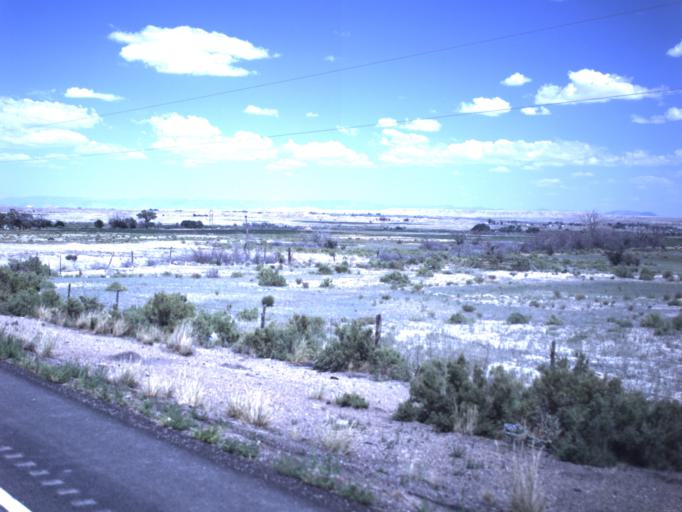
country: US
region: Utah
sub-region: Emery County
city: Huntington
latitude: 39.2899
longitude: -110.9698
